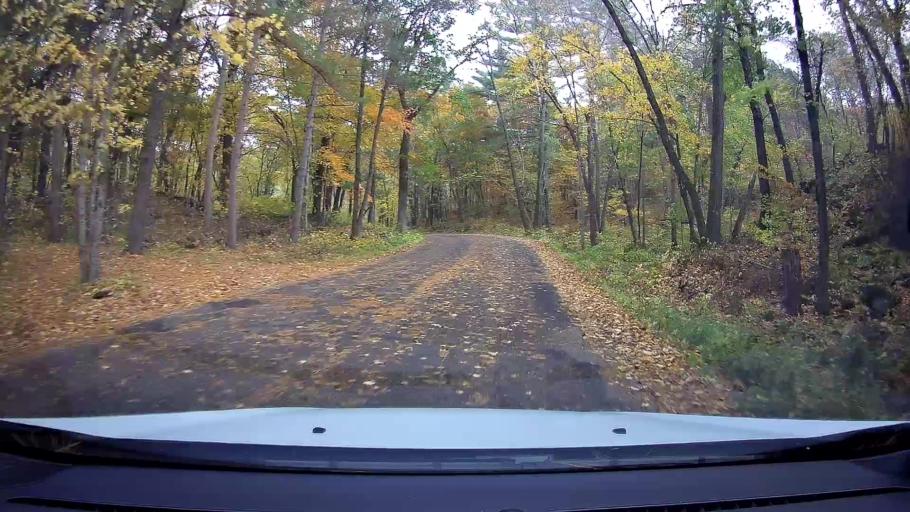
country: US
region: Wisconsin
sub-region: Polk County
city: Saint Croix Falls
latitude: 45.3926
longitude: -92.6509
